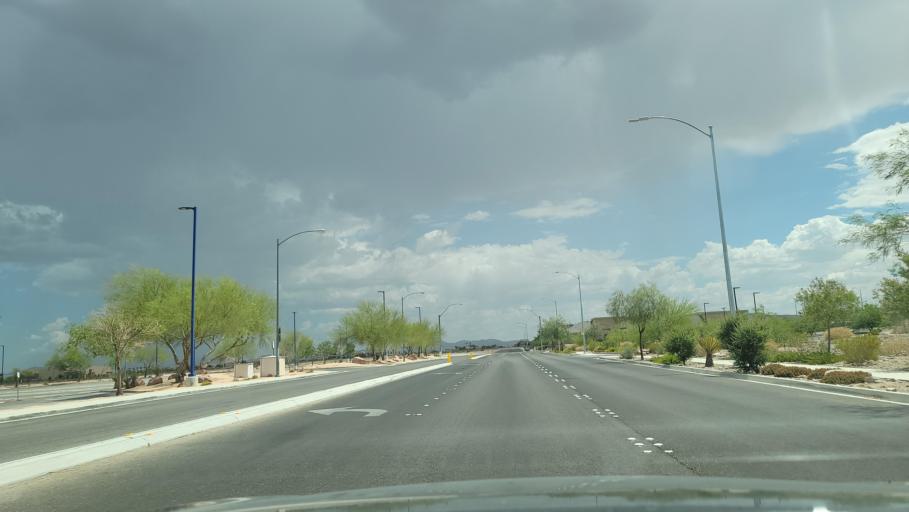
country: US
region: Nevada
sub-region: Clark County
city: Enterprise
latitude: 36.0499
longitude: -115.2702
